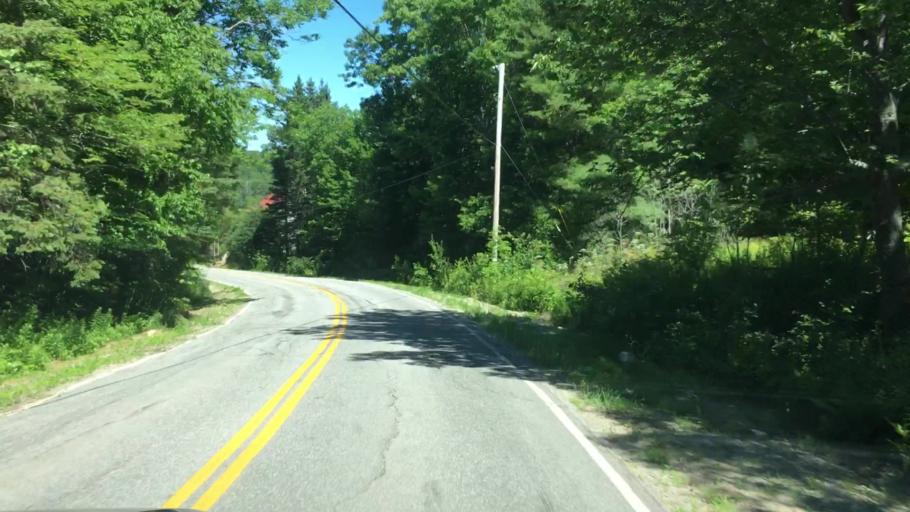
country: US
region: Maine
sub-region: Hancock County
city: Penobscot
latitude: 44.4233
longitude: -68.7066
